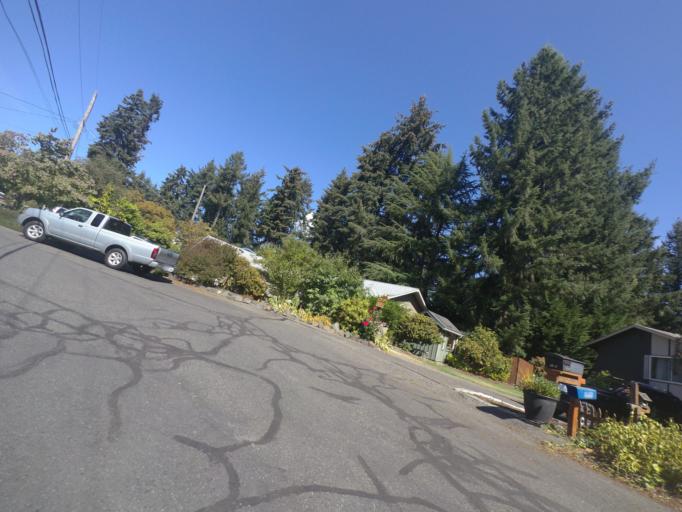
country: US
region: Washington
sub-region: Pierce County
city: Fircrest
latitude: 47.2177
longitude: -122.5148
